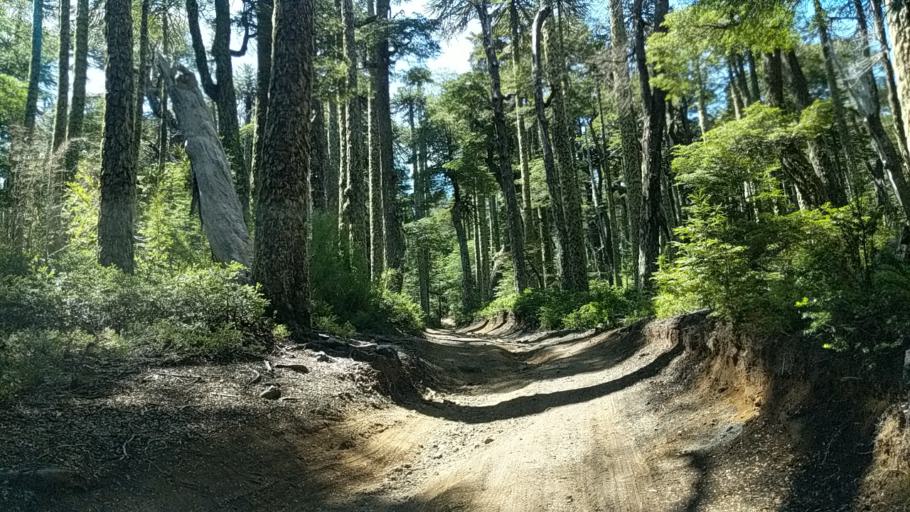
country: CL
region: Araucania
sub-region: Provincia de Cautin
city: Pucon
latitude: -39.4635
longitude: -71.8515
